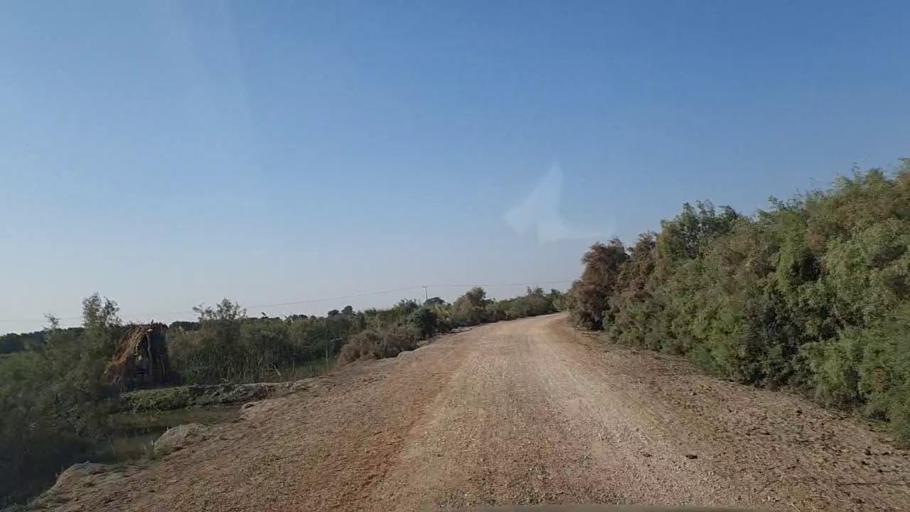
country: PK
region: Sindh
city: Mirpur Batoro
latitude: 24.7412
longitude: 68.3423
